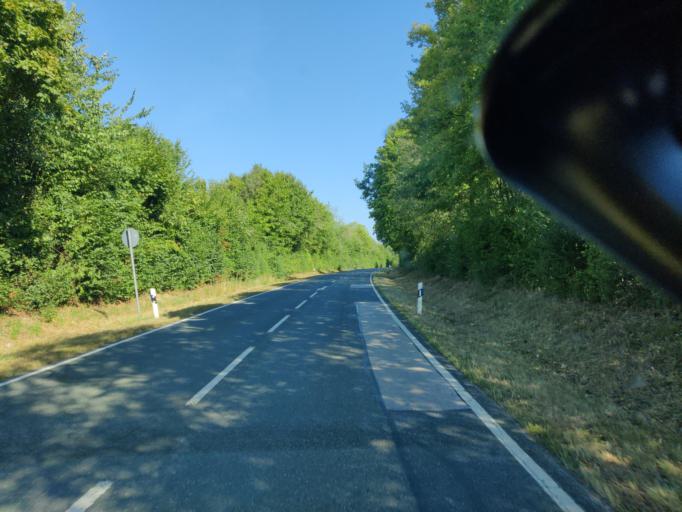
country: DE
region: Bavaria
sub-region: Regierungsbezirk Mittelfranken
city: Hilpoltstein
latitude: 49.1726
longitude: 11.2279
